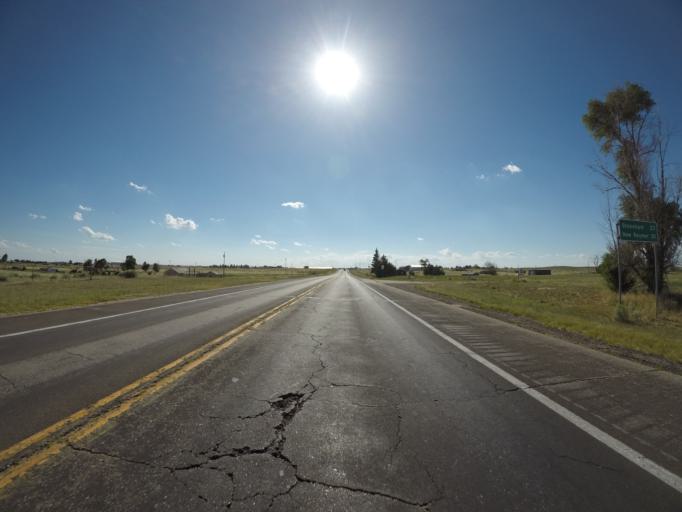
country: US
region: Colorado
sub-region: Logan County
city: Sterling
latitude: 40.6237
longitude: -103.2703
